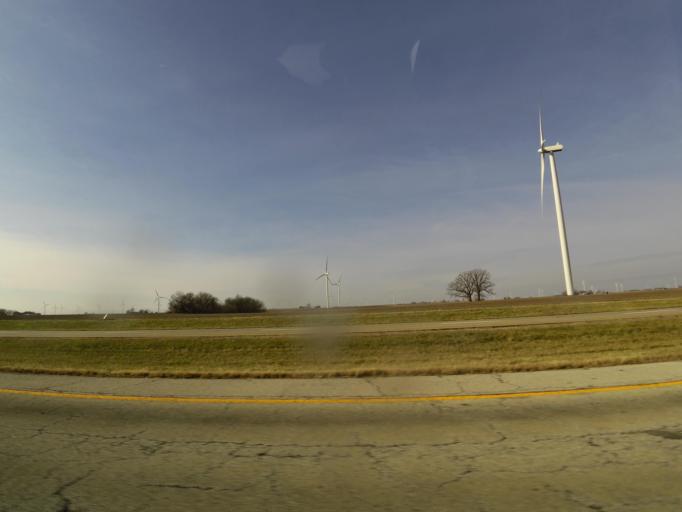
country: US
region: Illinois
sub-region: Macon County
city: Maroa
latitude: 40.0015
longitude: -88.9561
